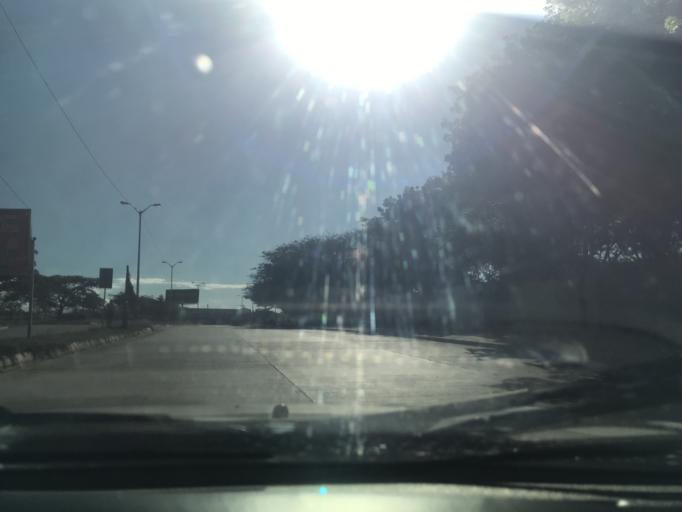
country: DO
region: Santiago
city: Santiago de los Caballeros
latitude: 19.4255
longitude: -70.6812
